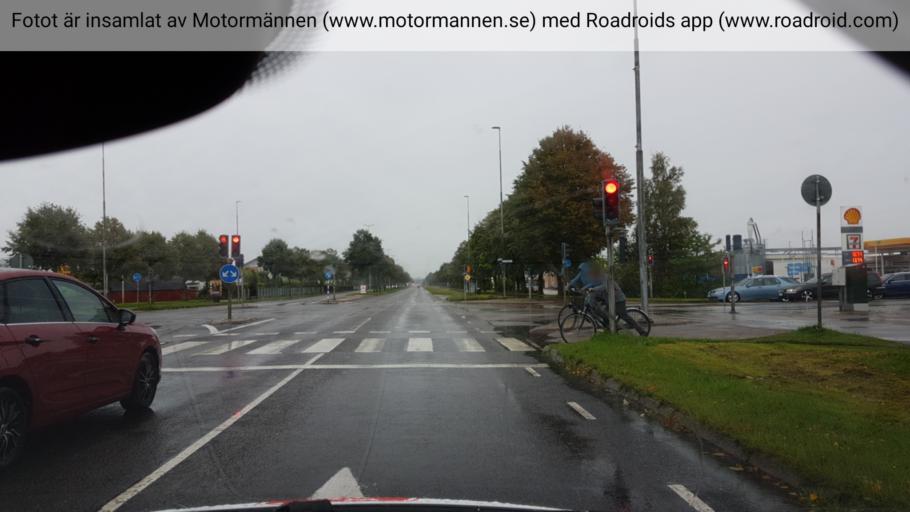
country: SE
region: Halland
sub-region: Halmstads Kommun
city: Halmstad
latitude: 56.6633
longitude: 12.8844
